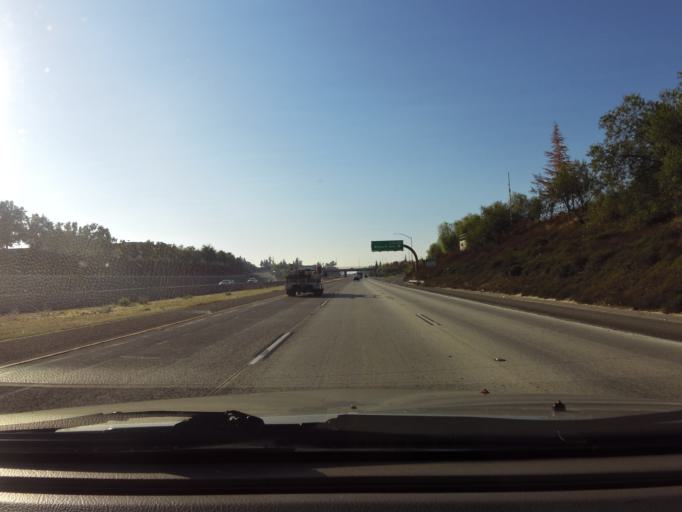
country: US
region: California
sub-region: Fresno County
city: Fresno
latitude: 36.8272
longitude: -119.7852
